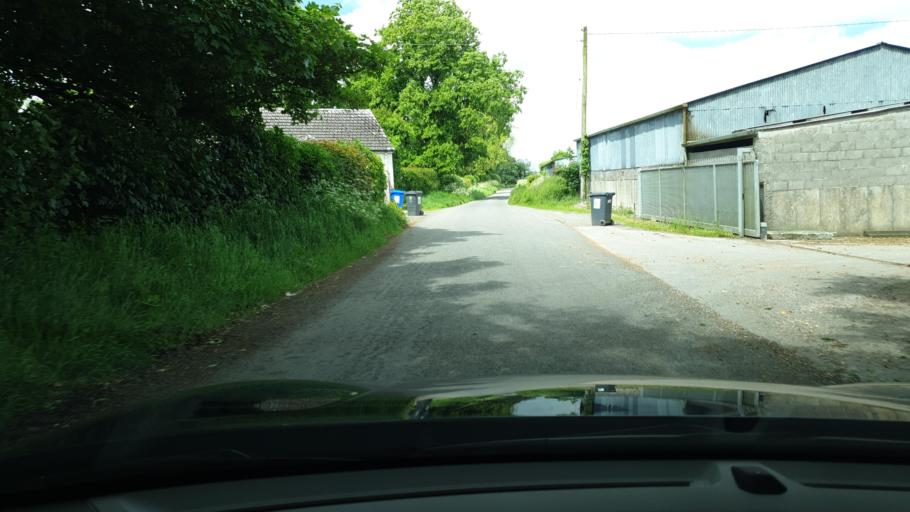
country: IE
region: Leinster
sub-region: An Mhi
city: Slane
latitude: 53.7370
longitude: -6.5594
